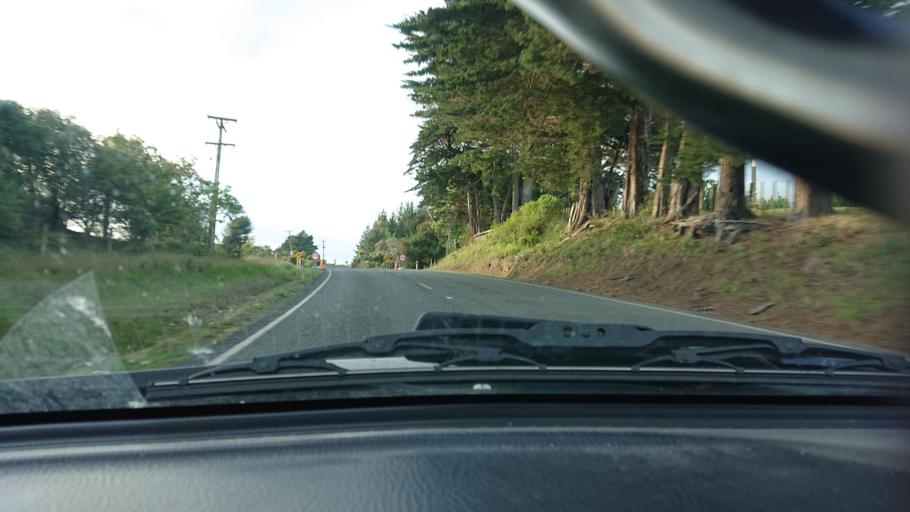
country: NZ
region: Auckland
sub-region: Auckland
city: Parakai
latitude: -36.5410
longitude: 174.4580
